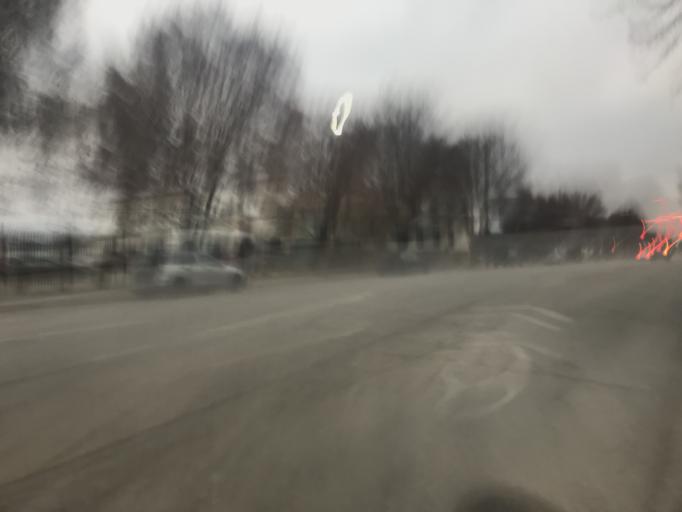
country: US
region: Kentucky
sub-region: Jefferson County
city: Louisville
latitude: 38.2580
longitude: -85.7682
